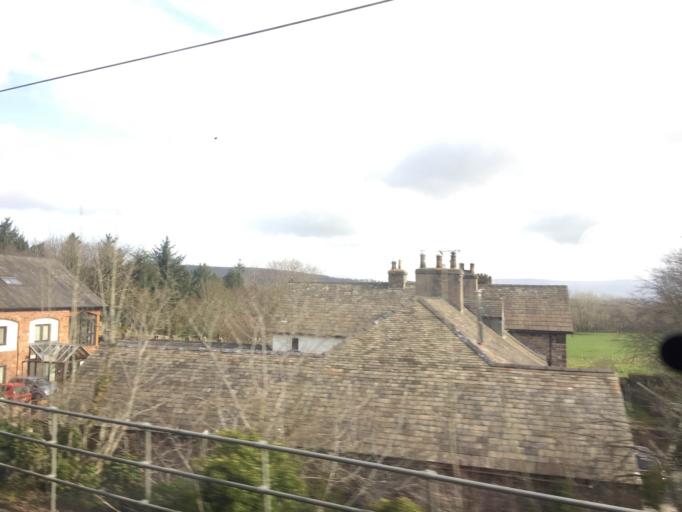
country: GB
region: England
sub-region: Cumbria
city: Penrith
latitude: 54.6447
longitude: -2.7615
